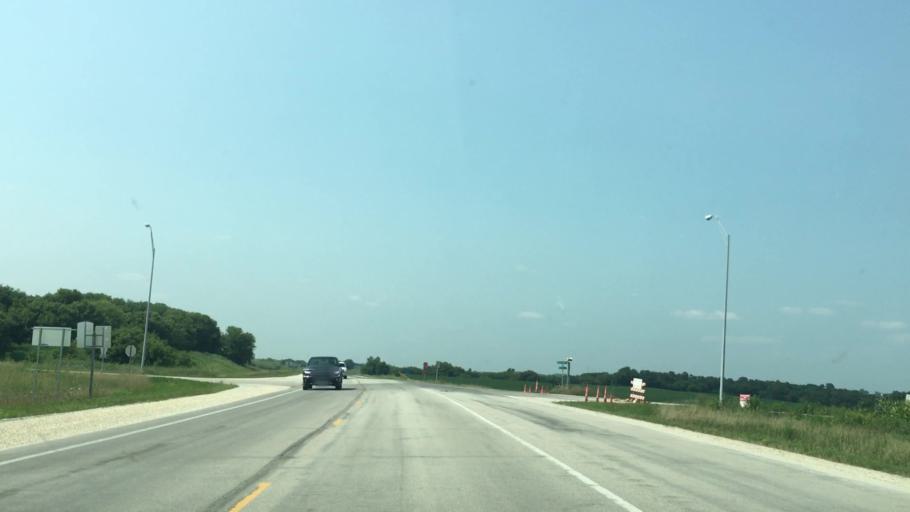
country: US
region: Iowa
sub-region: Winneshiek County
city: Decorah
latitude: 43.3673
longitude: -91.8061
